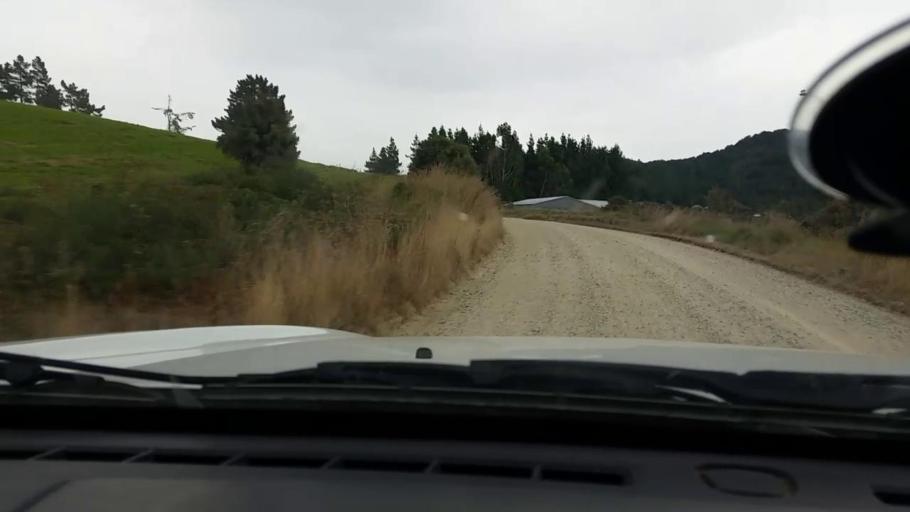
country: NZ
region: Otago
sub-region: Clutha District
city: Papatowai
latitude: -46.4608
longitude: 169.1202
